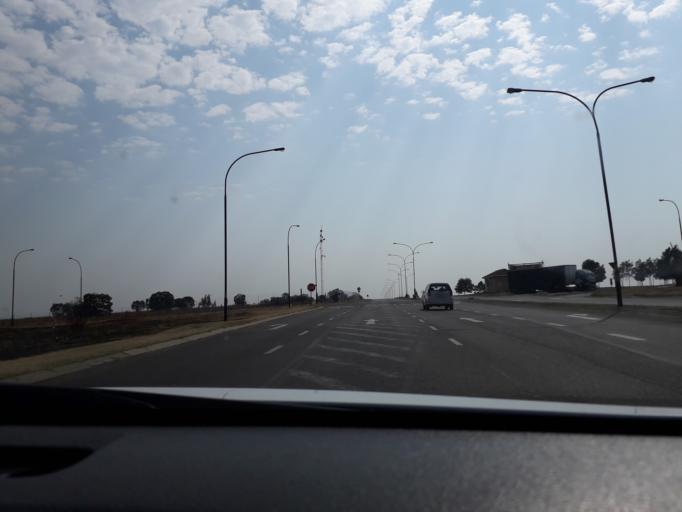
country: ZA
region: Gauteng
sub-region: Ekurhuleni Metropolitan Municipality
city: Tembisa
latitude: -26.0706
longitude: 28.2626
